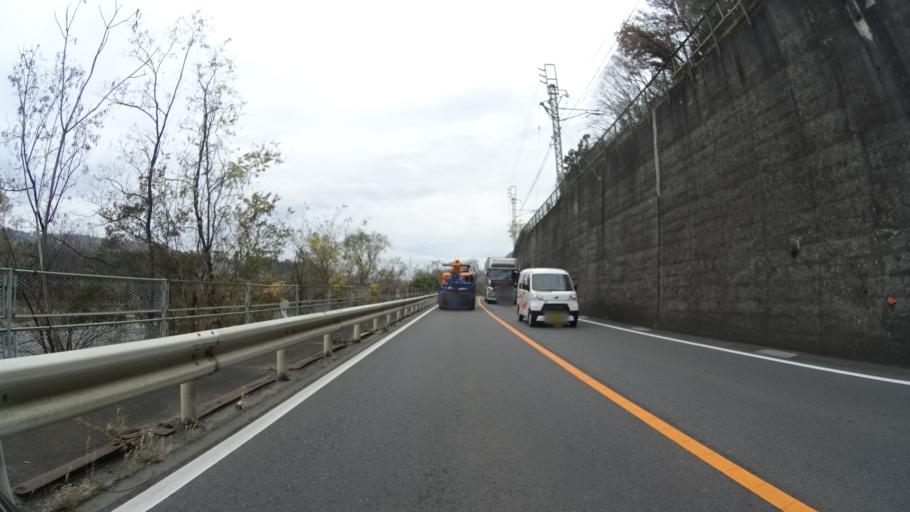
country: JP
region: Gunma
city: Numata
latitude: 36.6169
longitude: 139.0419
